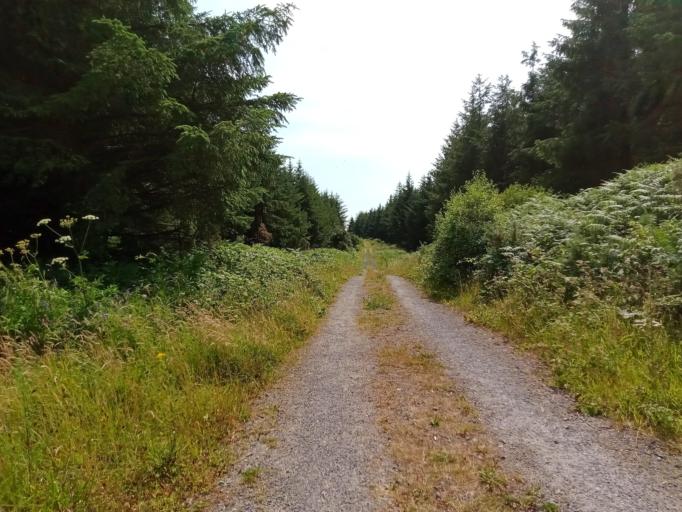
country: IE
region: Leinster
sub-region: Kilkenny
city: Ballyragget
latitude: 52.8049
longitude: -7.4537
